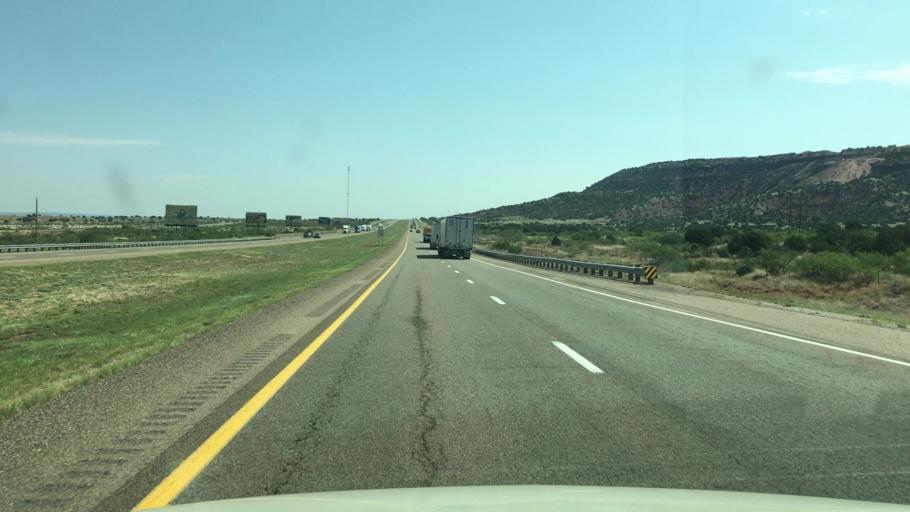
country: US
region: New Mexico
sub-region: Guadalupe County
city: Santa Rosa
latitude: 35.0369
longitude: -104.3964
